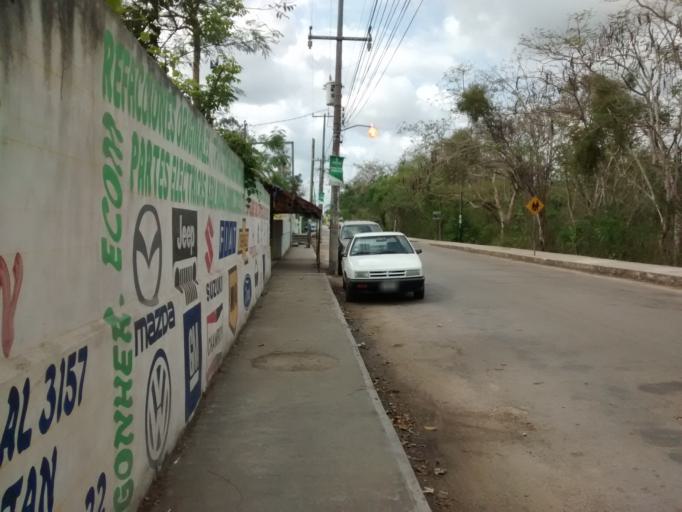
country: MX
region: Yucatan
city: Valladolid
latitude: 20.6906
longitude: -88.1810
